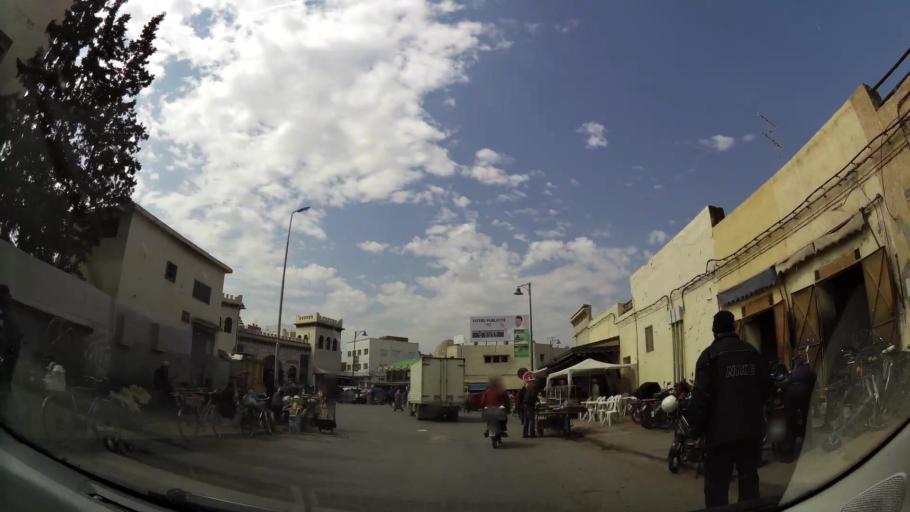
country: MA
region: Oriental
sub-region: Oujda-Angad
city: Oujda
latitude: 34.6805
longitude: -1.9076
